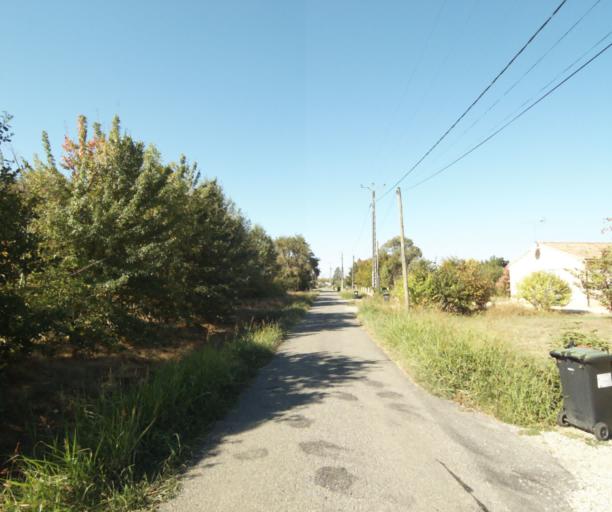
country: FR
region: Midi-Pyrenees
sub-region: Departement du Tarn-et-Garonne
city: Verdun-sur-Garonne
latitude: 43.8461
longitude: 1.2209
